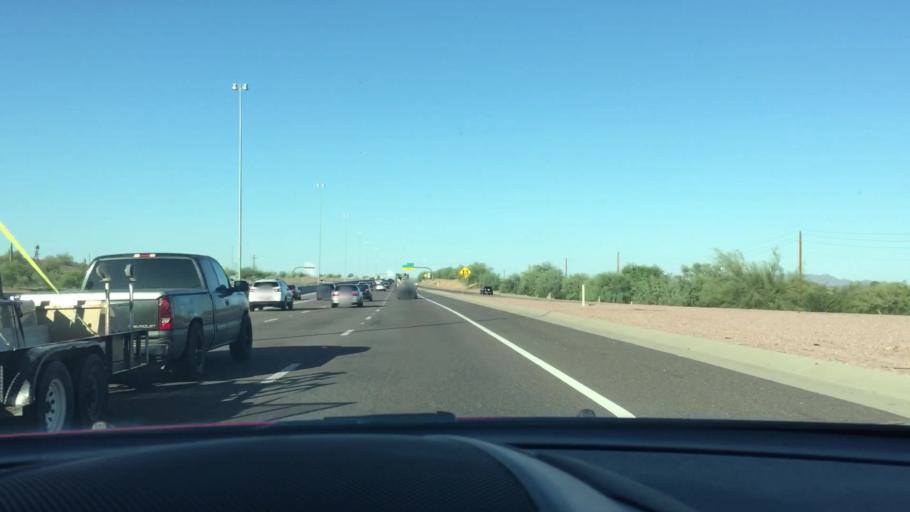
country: US
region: Arizona
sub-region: Maricopa County
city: Mesa
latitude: 33.4814
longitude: -111.7384
